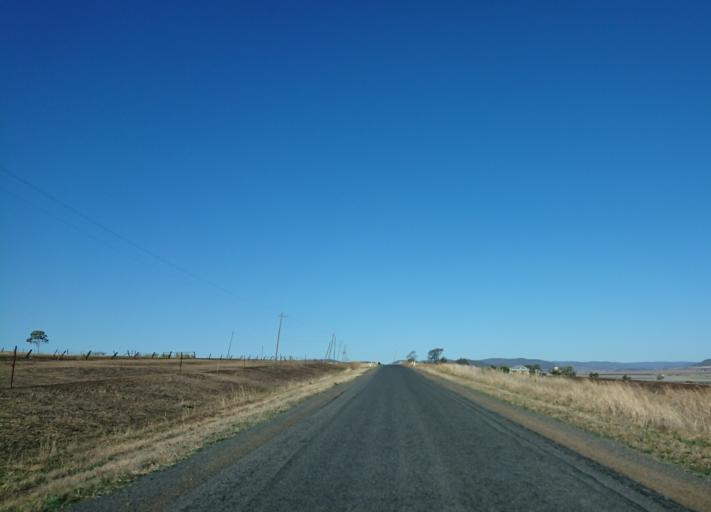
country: AU
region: Queensland
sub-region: Toowoomba
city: Top Camp
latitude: -27.8101
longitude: 151.9620
